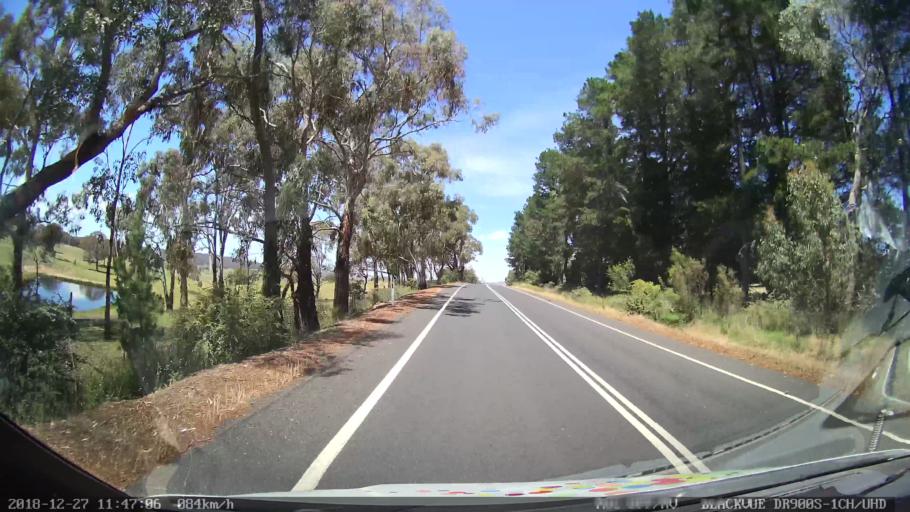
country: AU
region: New South Wales
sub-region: Bathurst Regional
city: Perthville
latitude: -33.5929
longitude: 149.4487
